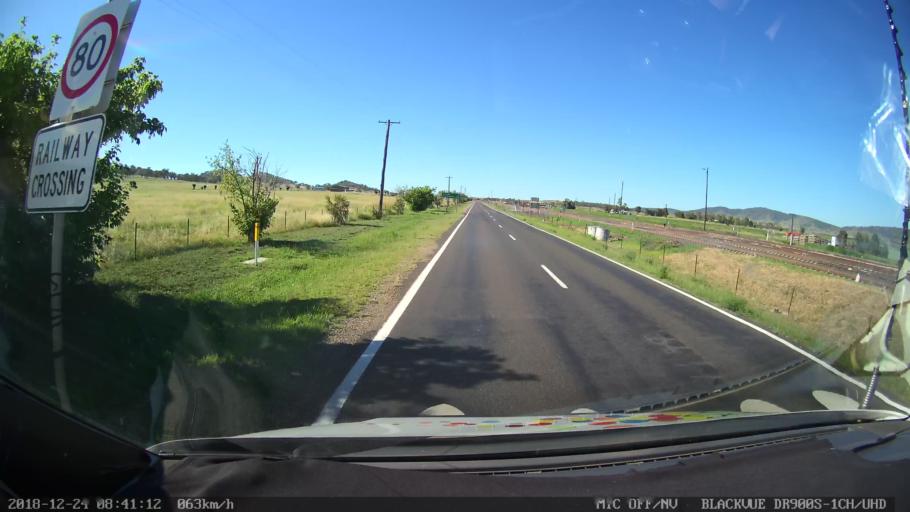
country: AU
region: New South Wales
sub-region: Liverpool Plains
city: Quirindi
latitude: -31.3609
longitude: 150.6453
